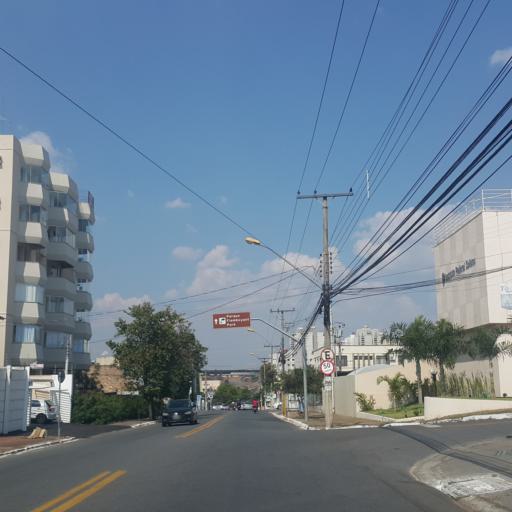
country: BR
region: Goias
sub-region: Goiania
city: Goiania
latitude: -16.6918
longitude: -49.2503
